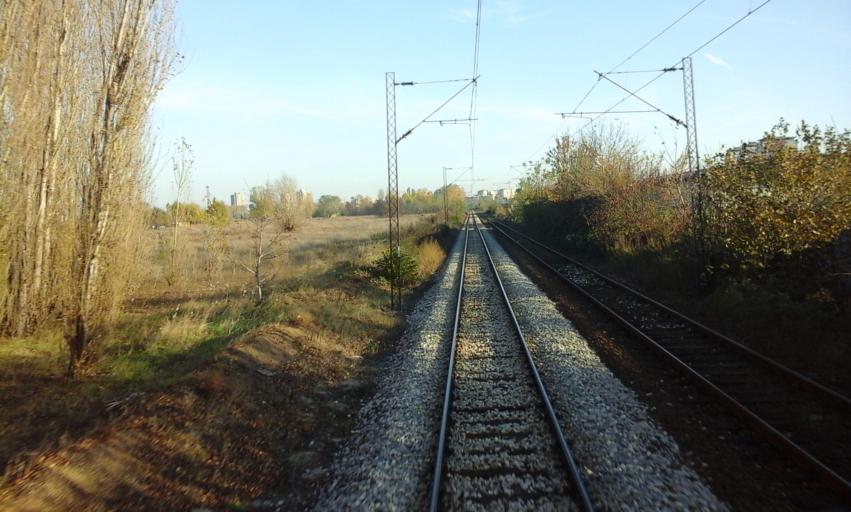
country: RS
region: Autonomna Pokrajina Vojvodina
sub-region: Juznobacki Okrug
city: Novi Sad
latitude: 45.2714
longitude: 19.8091
